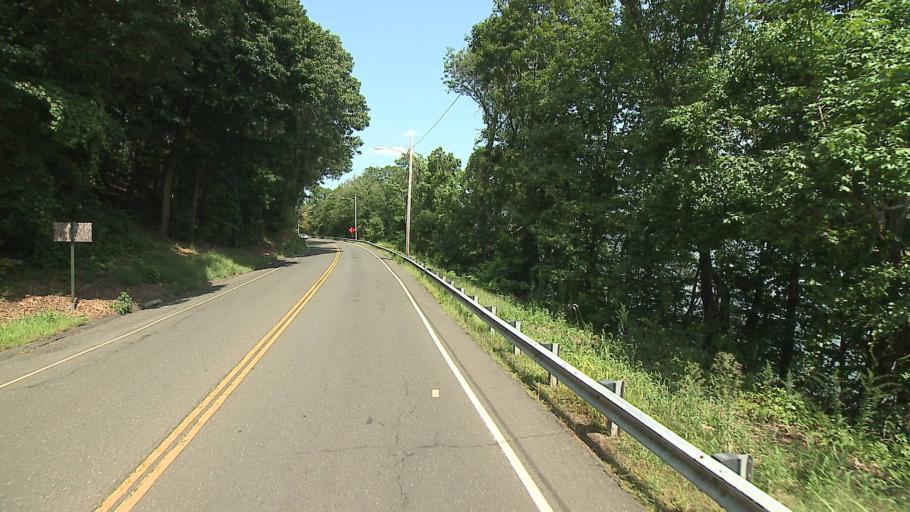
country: US
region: Connecticut
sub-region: New Haven County
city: City of Milford (balance)
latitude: 41.2373
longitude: -73.1067
